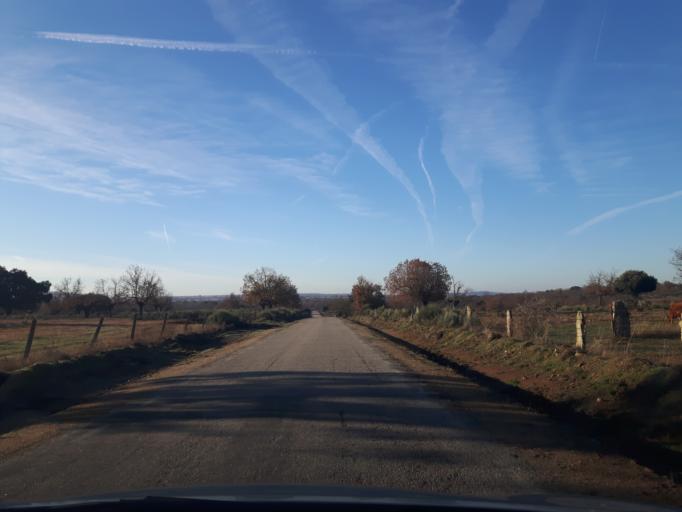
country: ES
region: Castille and Leon
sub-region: Provincia de Salamanca
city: Cerralbo
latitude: 40.9502
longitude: -6.6061
